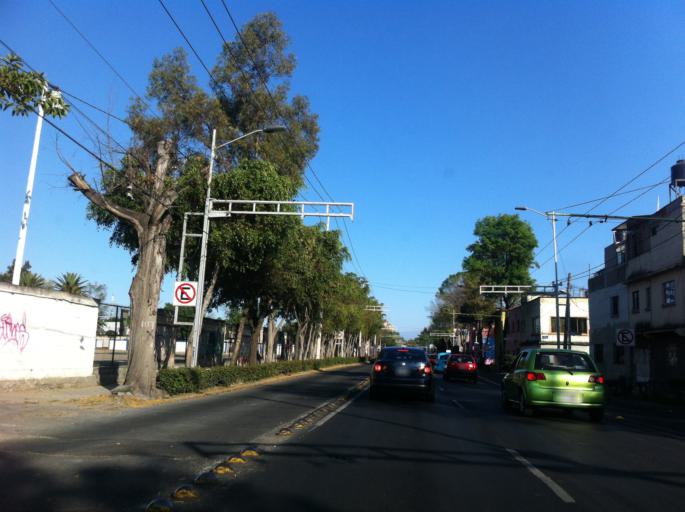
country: MX
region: Mexico City
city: Mexico City
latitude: 19.4138
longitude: -99.1206
